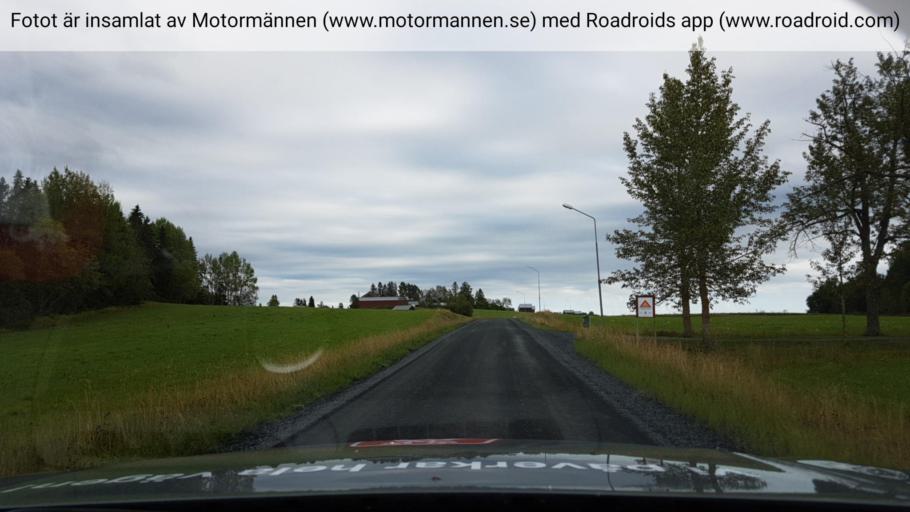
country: SE
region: Jaemtland
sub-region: Krokoms Kommun
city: Valla
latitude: 63.3650
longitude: 13.9578
